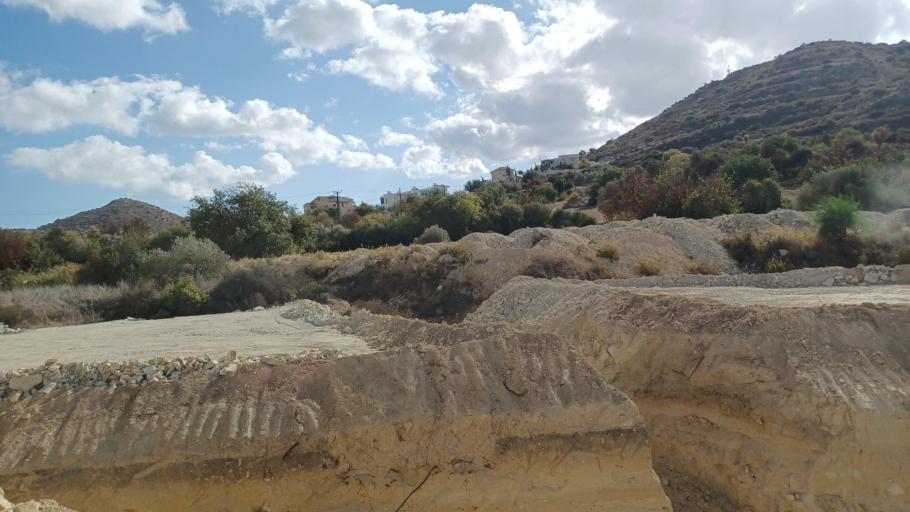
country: CY
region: Limassol
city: Pano Polemidia
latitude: 34.7443
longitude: 33.0011
